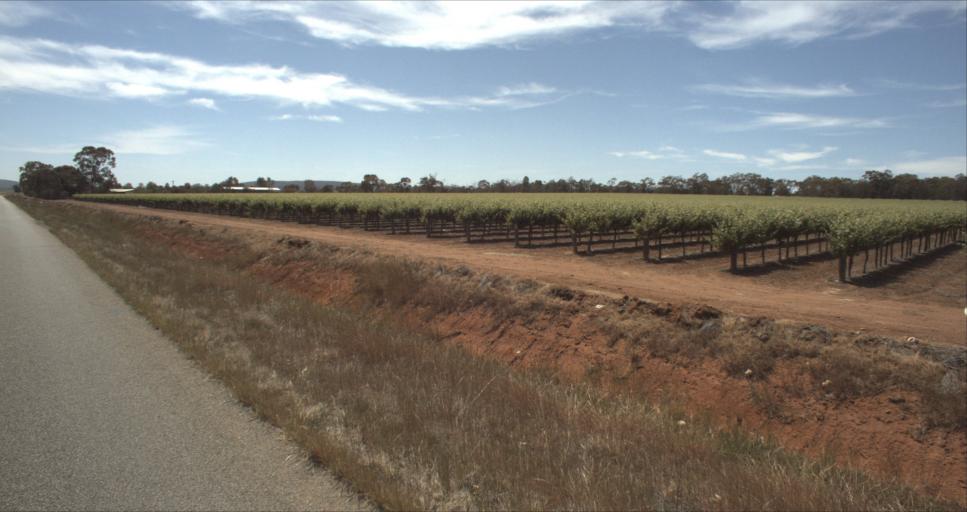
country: AU
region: New South Wales
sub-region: Leeton
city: Leeton
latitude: -34.5626
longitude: 146.4525
